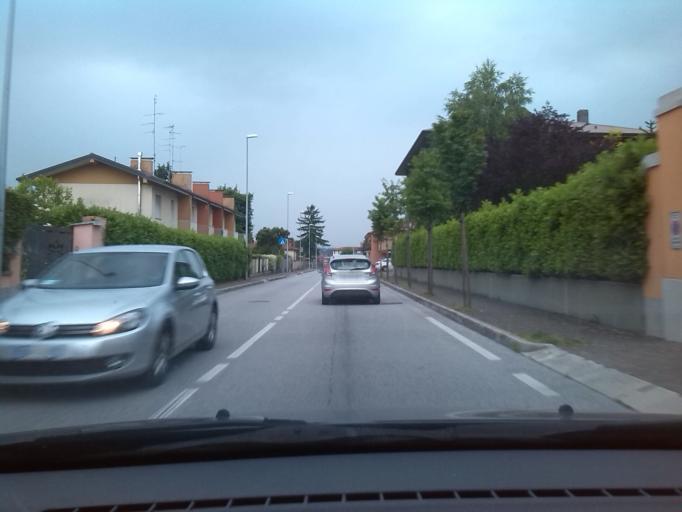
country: IT
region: Friuli Venezia Giulia
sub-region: Provincia di Udine
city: Majano
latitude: 46.1834
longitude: 13.0680
